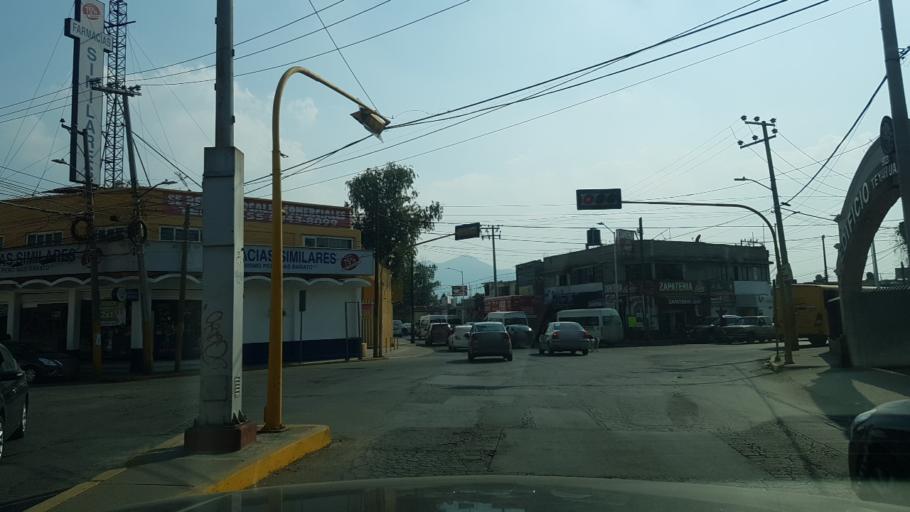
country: MX
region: Mexico
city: Santiago Teyahualco
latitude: 19.6613
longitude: -99.1280
